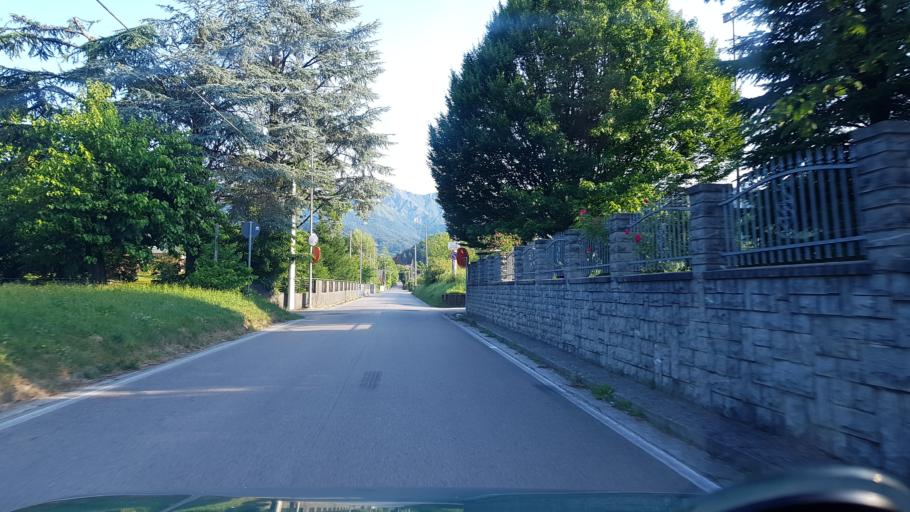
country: IT
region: Friuli Venezia Giulia
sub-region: Provincia di Udine
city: Tarcento
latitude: 46.2105
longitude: 13.2287
